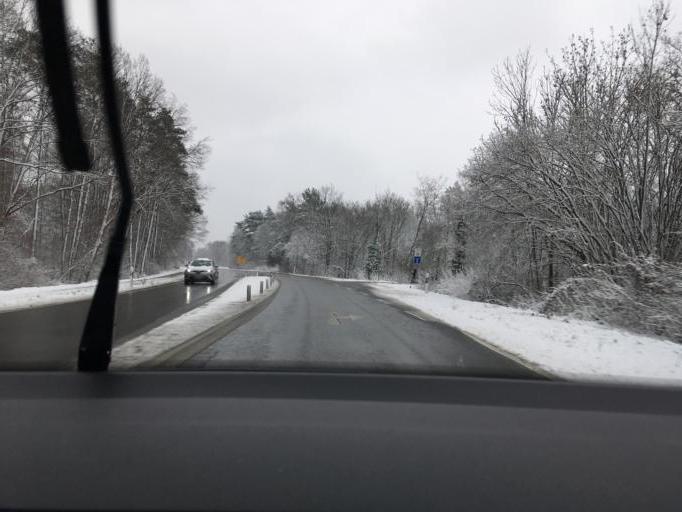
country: DE
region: Baden-Wuerttemberg
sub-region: Freiburg Region
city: Singen
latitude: 47.7615
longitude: 8.8733
